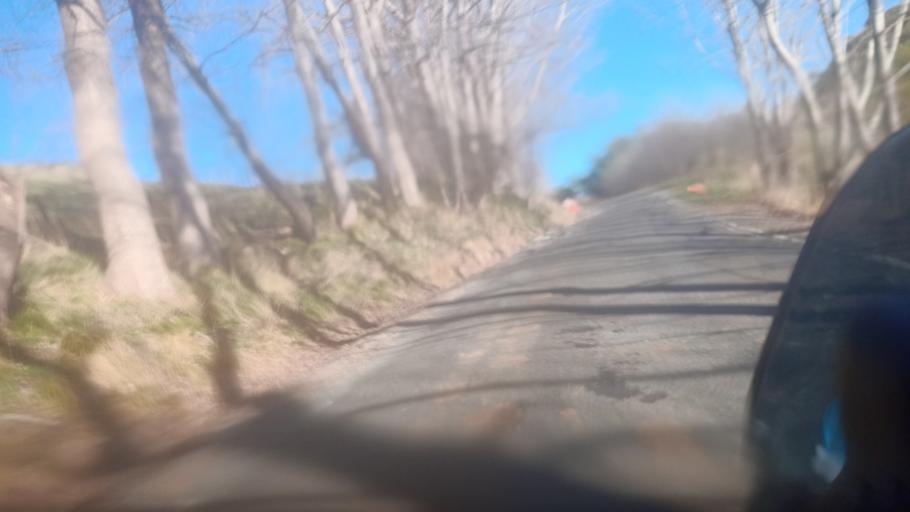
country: NZ
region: Gisborne
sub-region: Gisborne District
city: Gisborne
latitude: -38.5647
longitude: 177.6066
